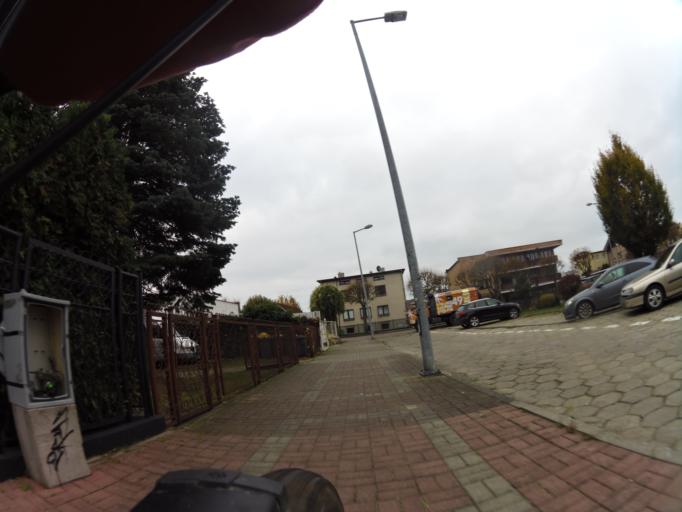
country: PL
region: Pomeranian Voivodeship
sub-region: Powiat pucki
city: Jastarnia
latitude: 54.6993
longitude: 18.6805
